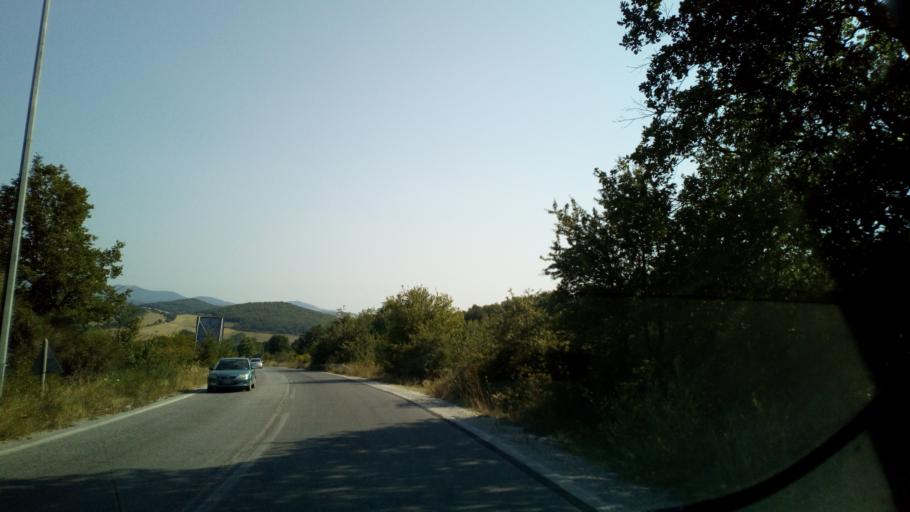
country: GR
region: Central Macedonia
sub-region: Nomos Chalkidikis
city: Polygyros
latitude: 40.4864
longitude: 23.4002
